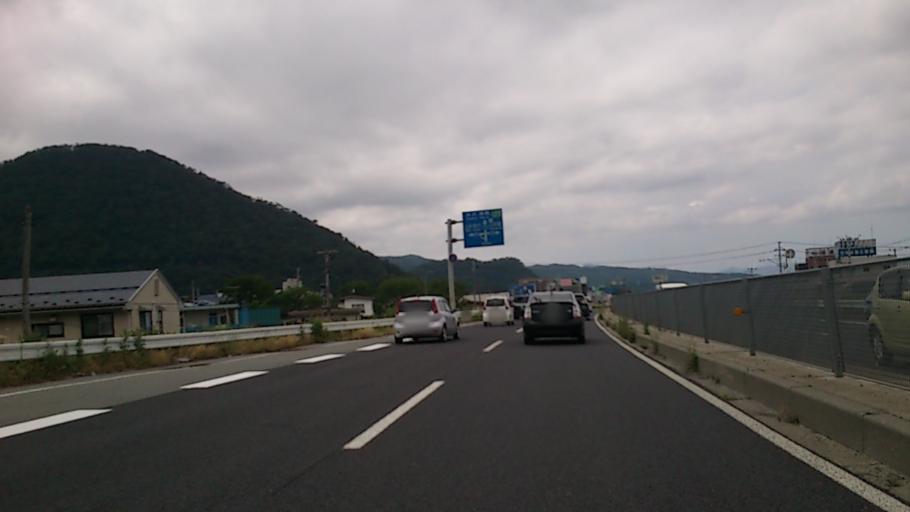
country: JP
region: Yamagata
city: Yamagata-shi
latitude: 38.2465
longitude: 140.3564
